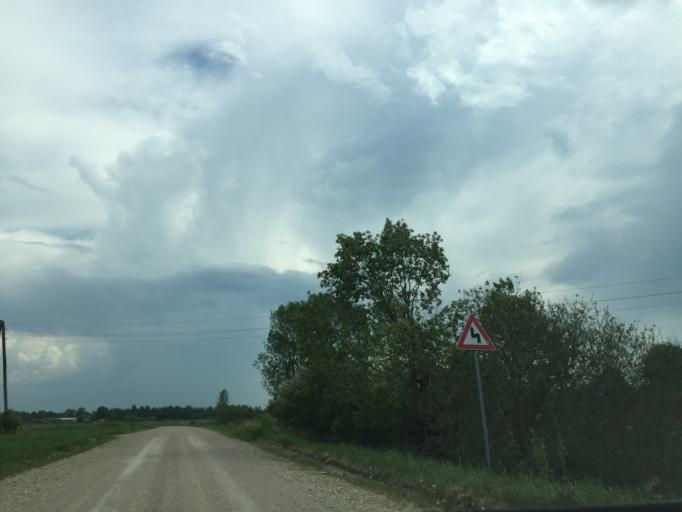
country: LV
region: Livani
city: Livani
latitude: 56.5507
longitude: 26.2292
